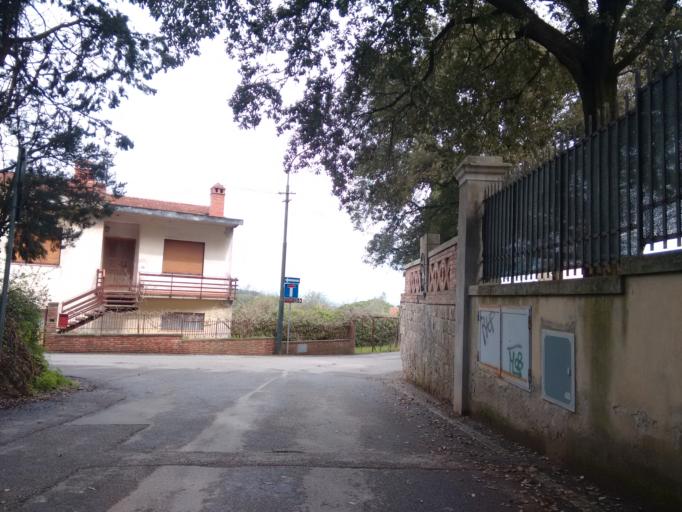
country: IT
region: Tuscany
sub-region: Province of Florence
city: Strada in Chianti
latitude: 43.6600
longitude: 11.2977
